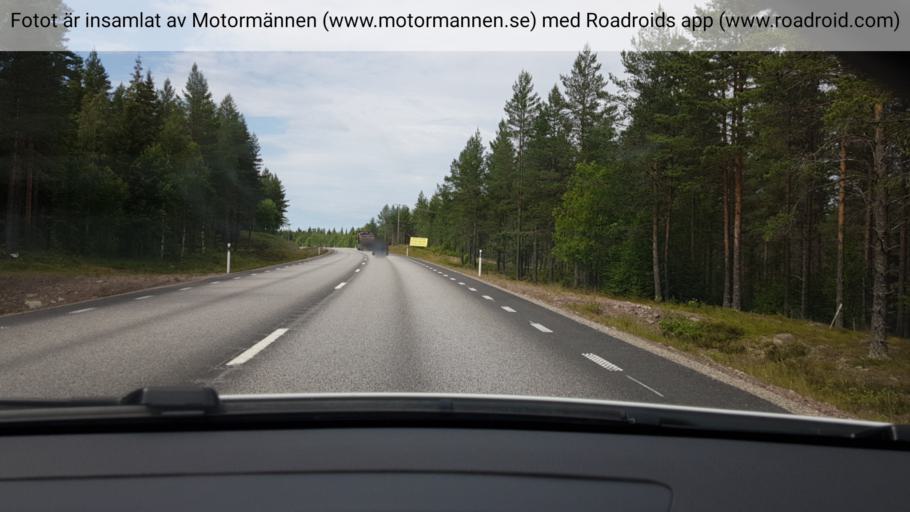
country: SE
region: Dalarna
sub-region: Rattviks Kommun
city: Raettvik
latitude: 60.8198
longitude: 15.2573
